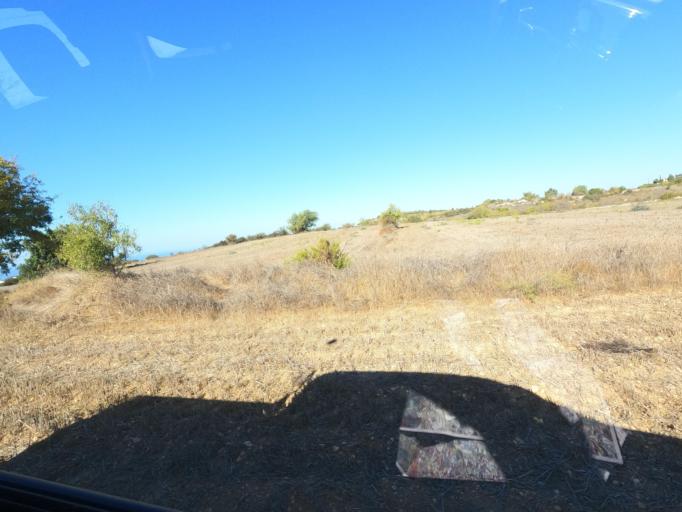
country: CY
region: Pafos
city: Mesogi
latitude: 34.8004
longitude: 32.4917
